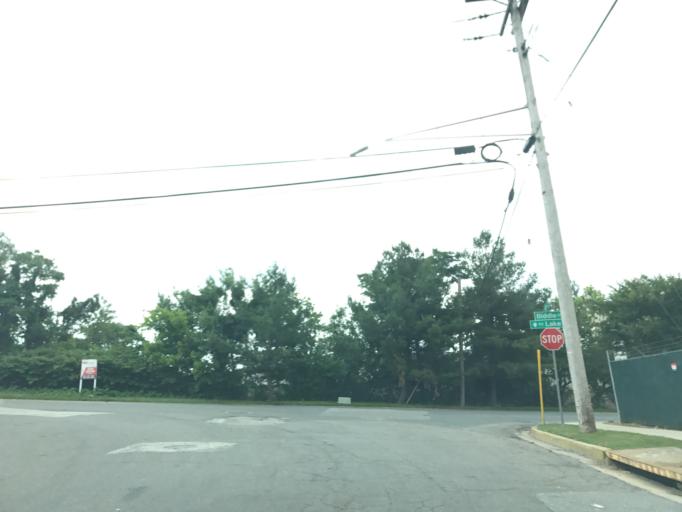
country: US
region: Maryland
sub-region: Baltimore County
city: Rosedale
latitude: 39.3095
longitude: -76.5263
